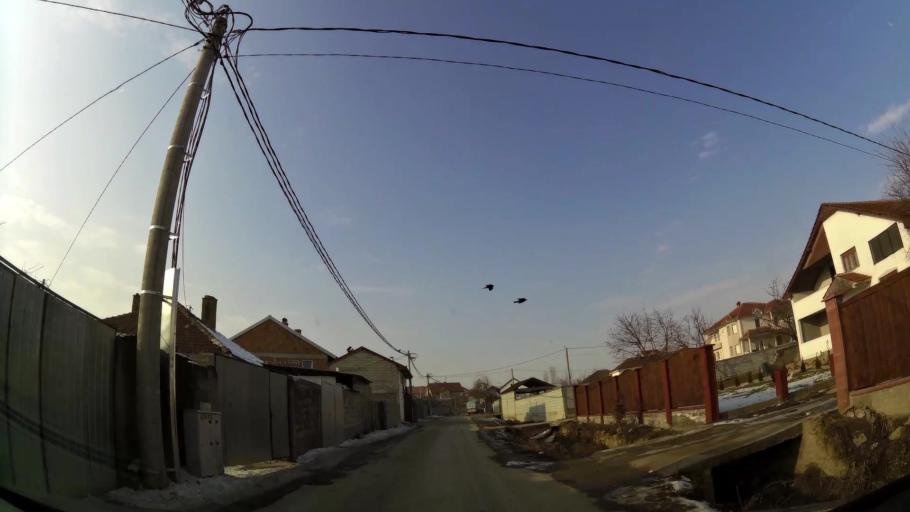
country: MK
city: Creshevo
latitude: 42.0214
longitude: 21.5018
